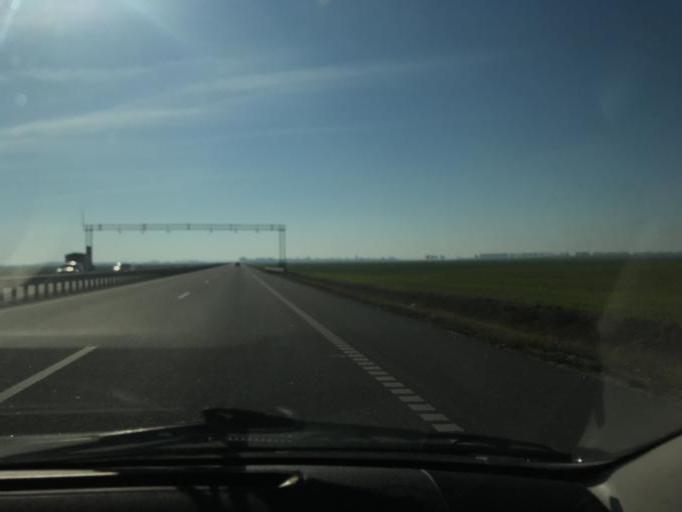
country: BY
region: Minsk
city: Slutsk
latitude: 53.1732
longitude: 27.5515
